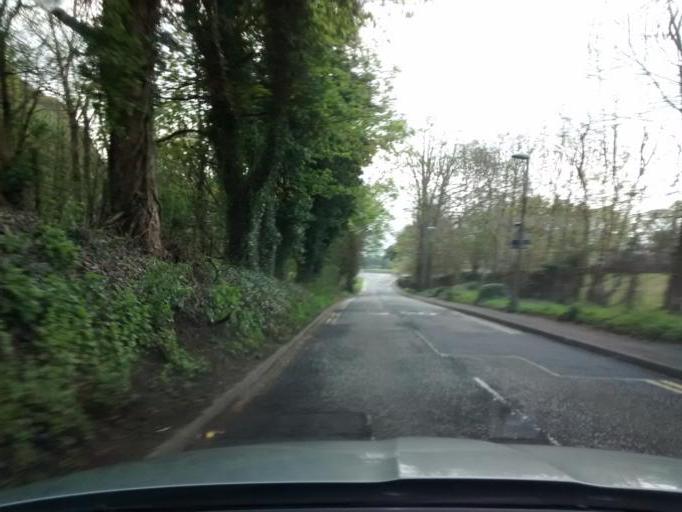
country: GB
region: Scotland
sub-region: Edinburgh
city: Colinton
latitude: 55.9192
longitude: -3.2343
